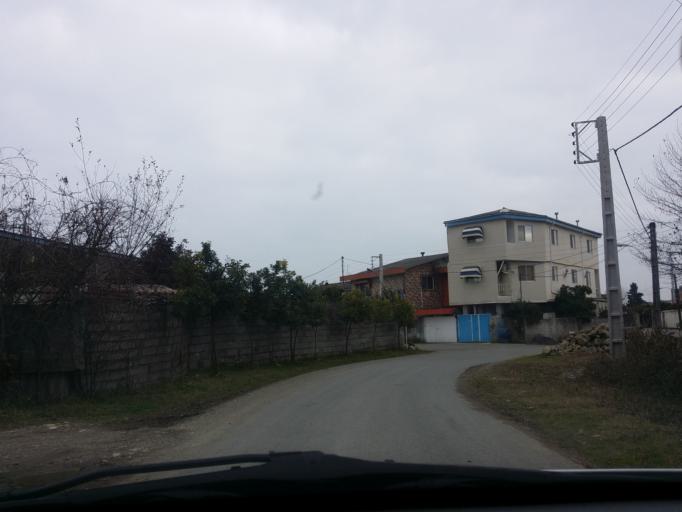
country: IR
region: Mazandaran
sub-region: Nowshahr
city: Nowshahr
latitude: 36.6525
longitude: 51.4734
